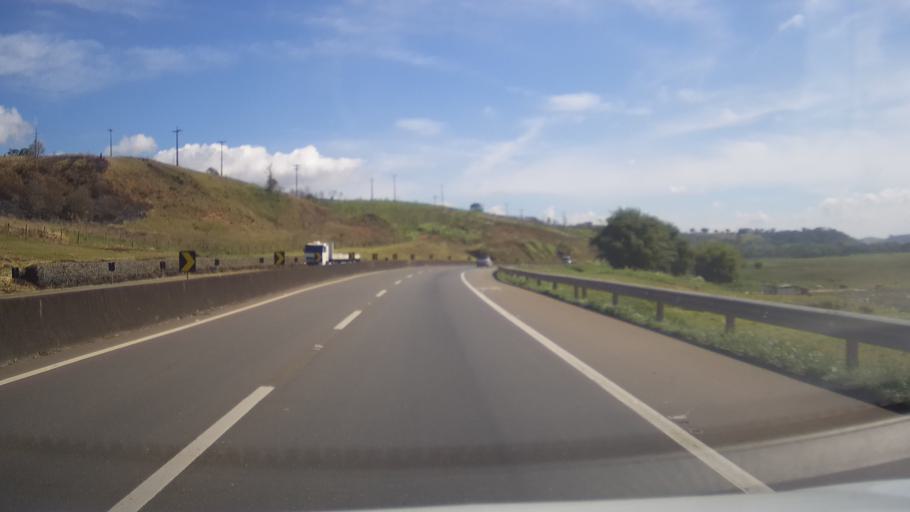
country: BR
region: Minas Gerais
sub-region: Cambui
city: Cambui
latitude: -22.5465
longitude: -46.0404
